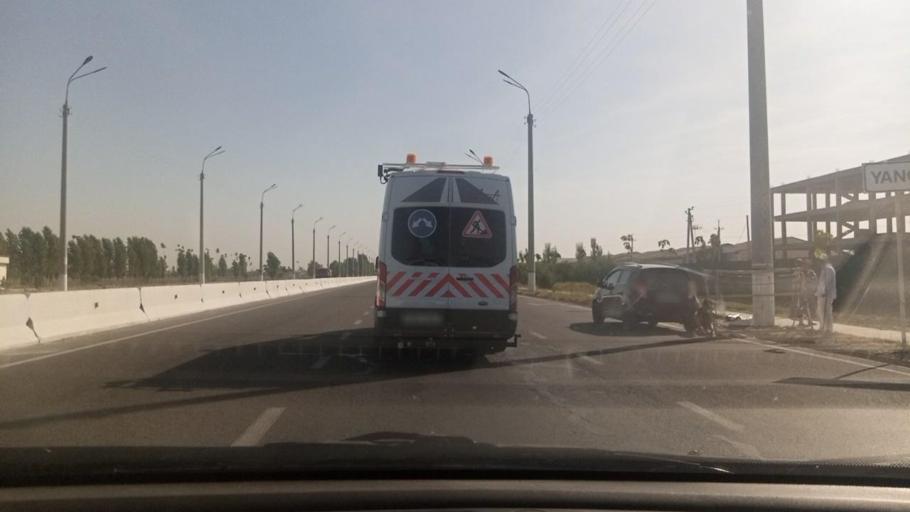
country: UZ
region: Toshkent Shahri
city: Bektemir
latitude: 41.2055
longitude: 69.3373
